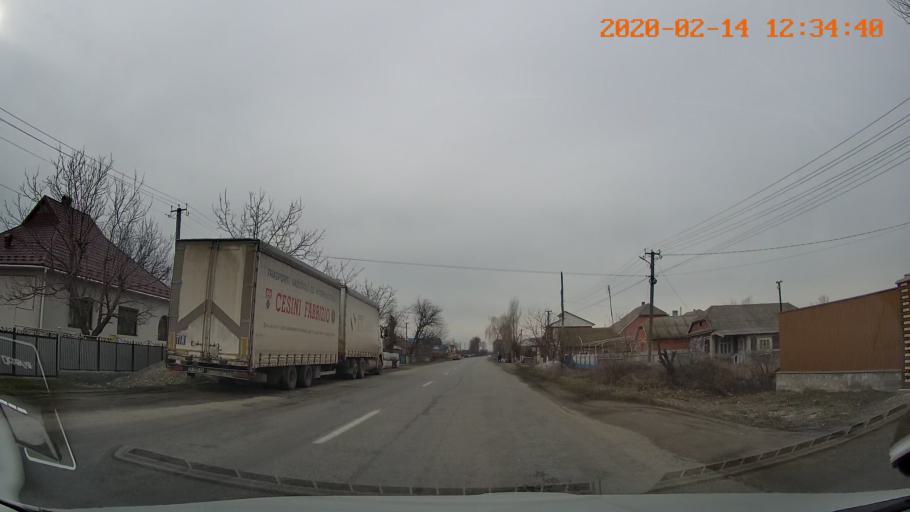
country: RO
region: Botosani
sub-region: Comuna Darabani
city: Bajura
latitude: 48.2284
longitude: 26.5259
